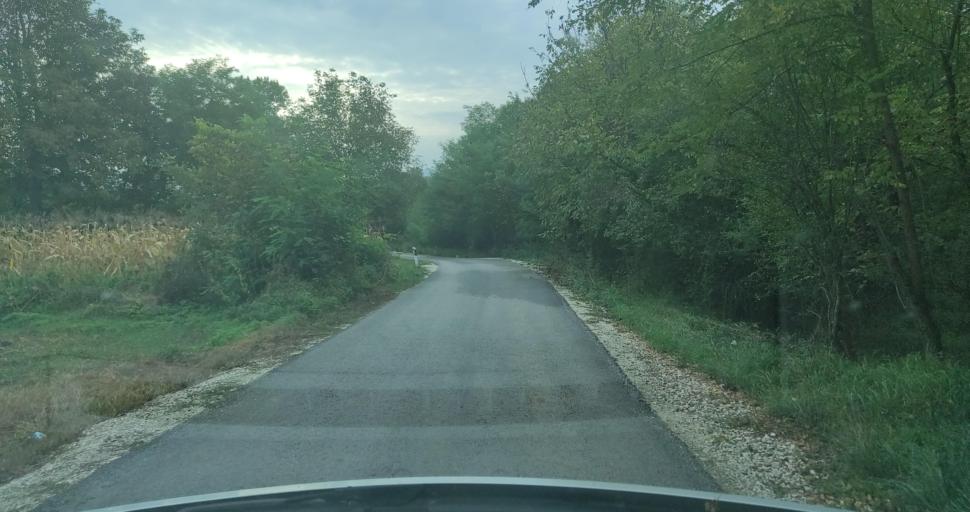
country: RS
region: Central Serbia
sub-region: Pcinjski Okrug
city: Vladicin Han
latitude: 42.6719
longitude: 22.0220
